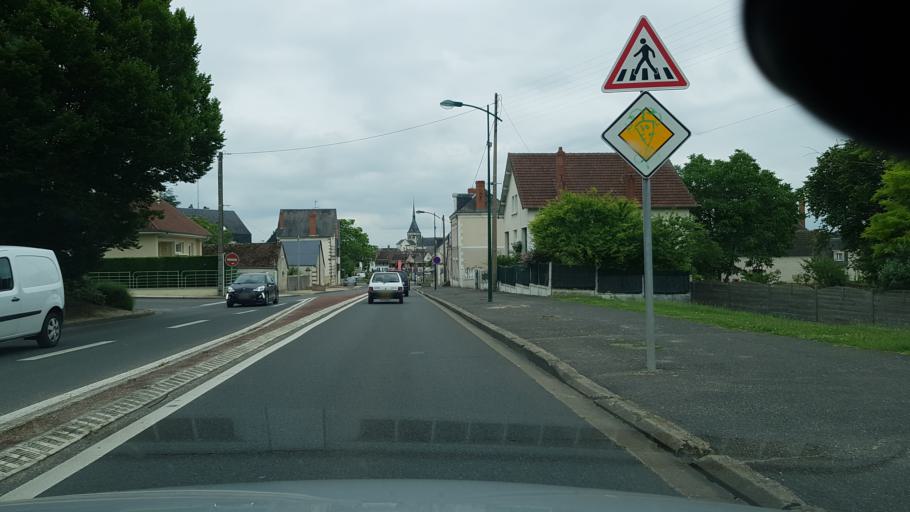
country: FR
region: Centre
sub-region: Departement du Loir-et-Cher
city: Selles-sur-Cher
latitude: 47.2789
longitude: 1.5488
